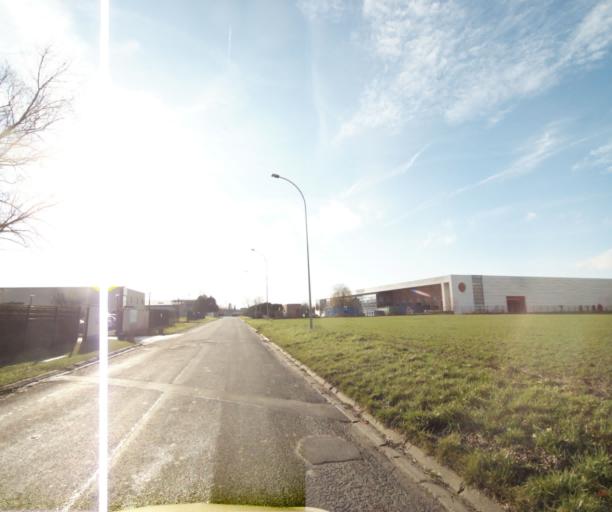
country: FR
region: Nord-Pas-de-Calais
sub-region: Departement du Nord
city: Saultain
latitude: 50.3458
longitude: 3.5650
